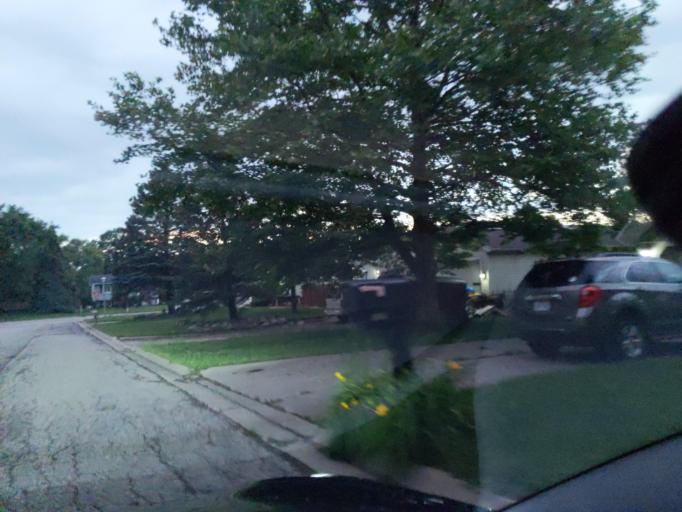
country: US
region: Michigan
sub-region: Eaton County
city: Dimondale
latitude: 42.6575
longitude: -84.5854
